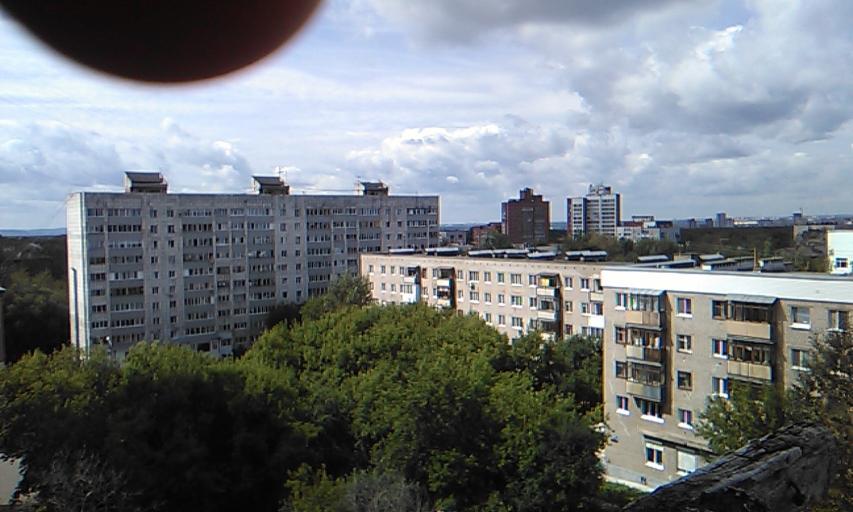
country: RU
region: Perm
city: Perm
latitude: 57.9780
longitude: 56.1824
